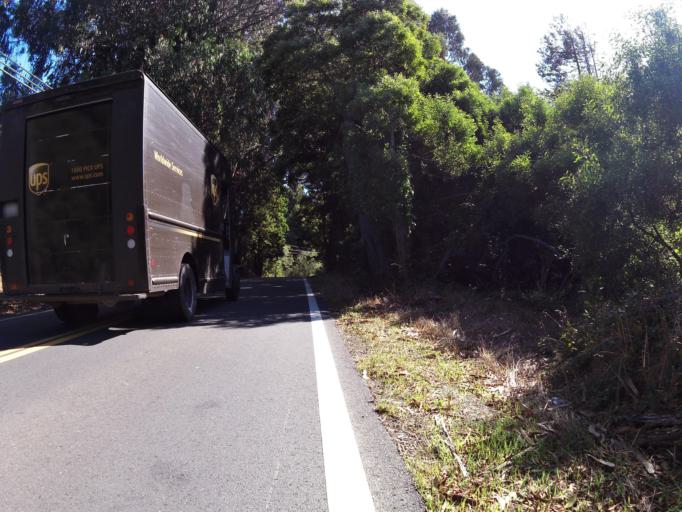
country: US
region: California
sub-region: Mendocino County
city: Fort Bragg
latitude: 39.5236
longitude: -123.7611
